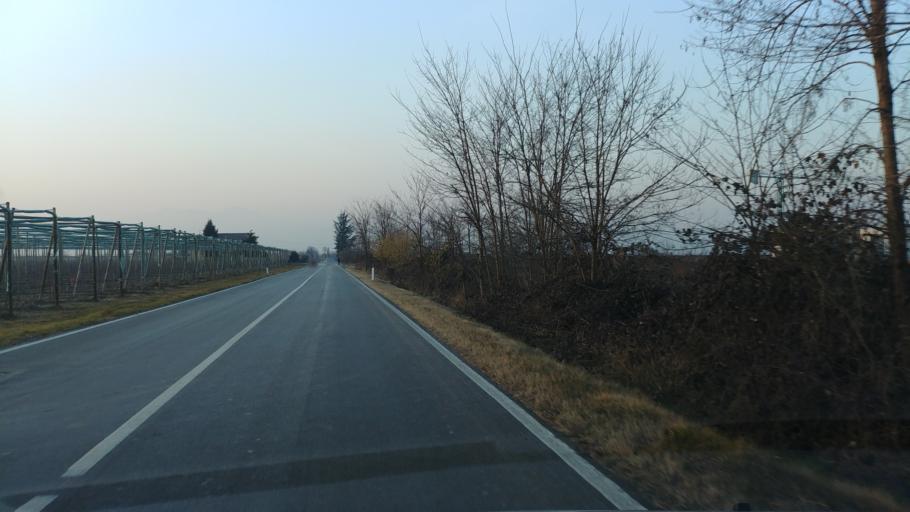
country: IT
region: Piedmont
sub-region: Provincia di Cuneo
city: Roata Rossi
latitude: 44.4194
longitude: 7.5335
